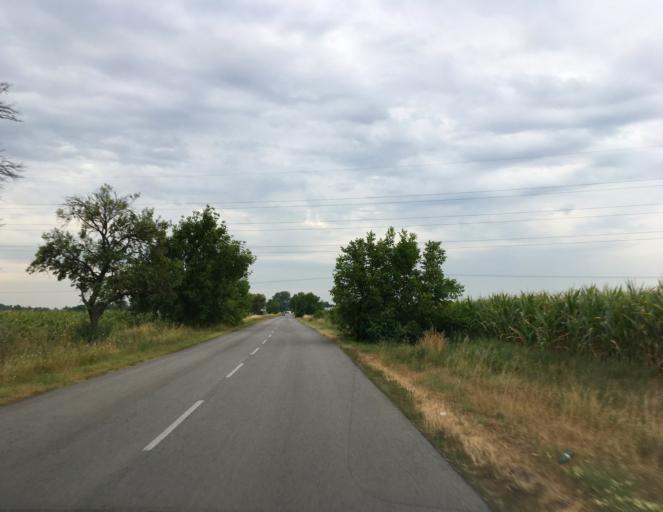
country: SK
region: Trnavsky
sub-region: Okres Dunajska Streda
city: Velky Meder
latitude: 47.9284
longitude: 17.7011
